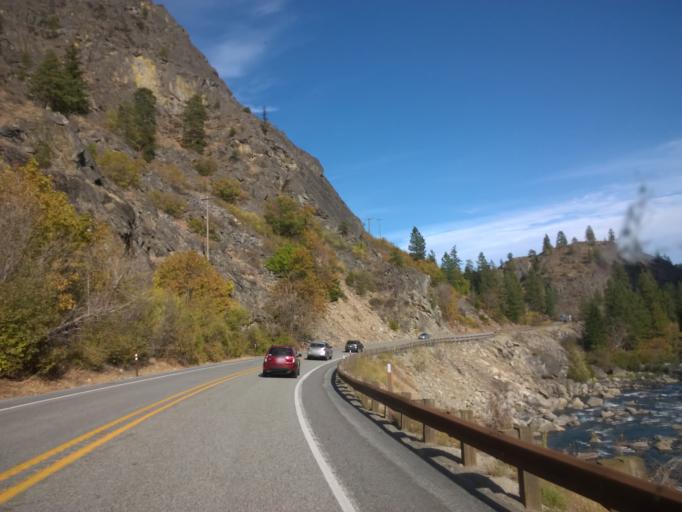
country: US
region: Washington
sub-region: Chelan County
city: Leavenworth
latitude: 47.5877
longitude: -120.6848
